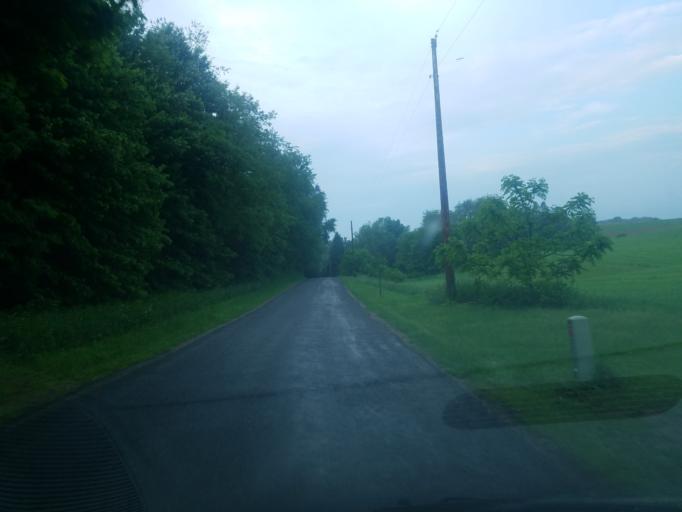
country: US
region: Ohio
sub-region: Stark County
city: Minerva
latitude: 40.7700
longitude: -80.9557
